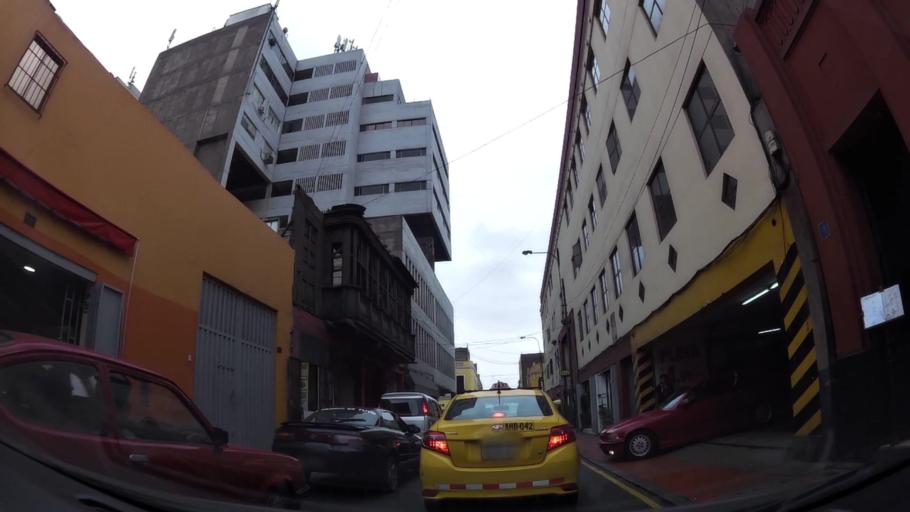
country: PE
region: Lima
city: Lima
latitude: -12.0506
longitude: -77.0301
